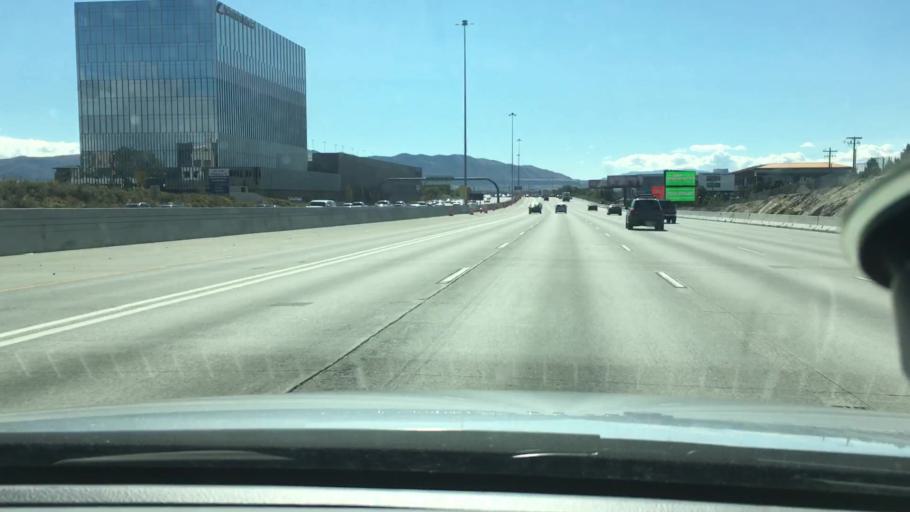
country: US
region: Utah
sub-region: Salt Lake County
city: Sandy City
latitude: 40.5747
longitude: -111.9003
